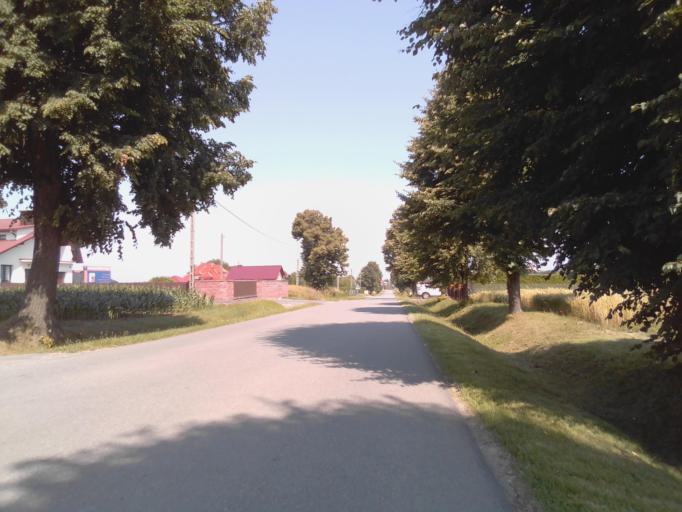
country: PL
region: Subcarpathian Voivodeship
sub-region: Powiat ropczycko-sedziszowski
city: Sedziszow Malopolski
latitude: 50.0567
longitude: 21.6687
